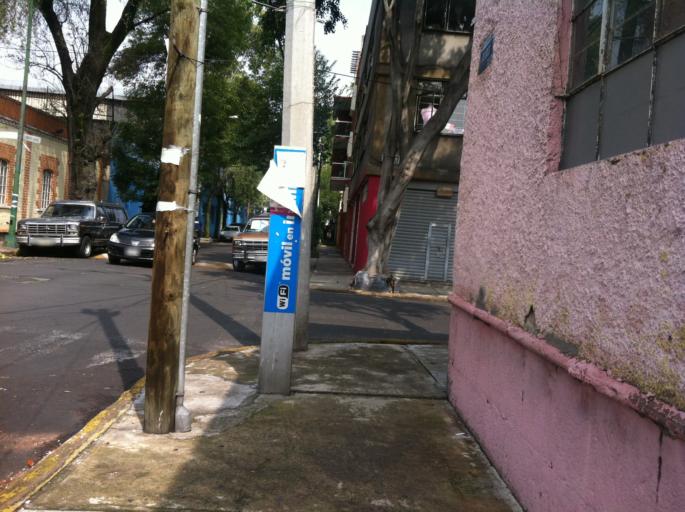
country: MX
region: Mexico City
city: Azcapotzalco
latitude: 19.4602
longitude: -99.1826
